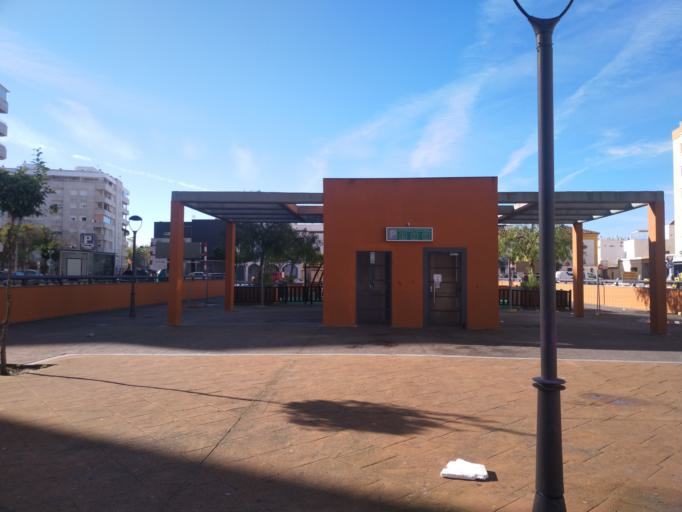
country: ES
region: Andalusia
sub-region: Provincia de Cadiz
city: San Fernando
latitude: 36.4686
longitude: -6.2001
